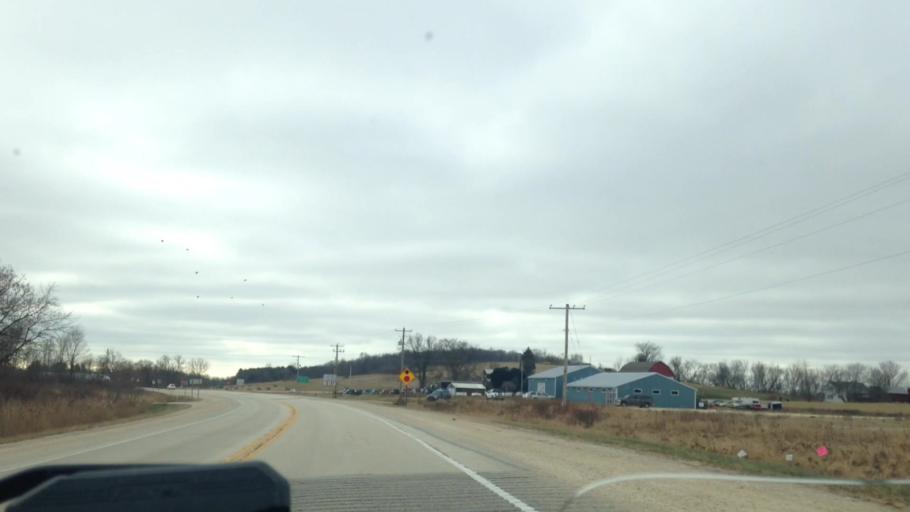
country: US
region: Wisconsin
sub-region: Dodge County
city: Mayville
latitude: 43.4457
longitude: -88.5442
